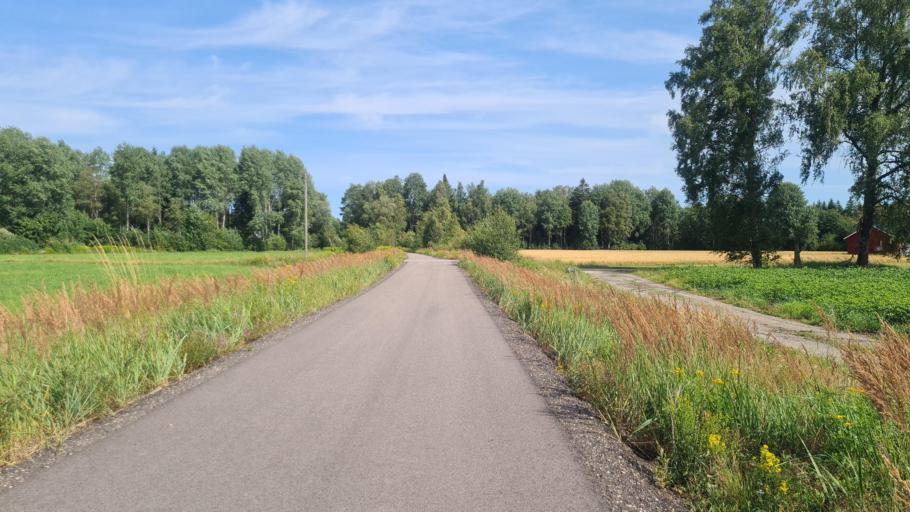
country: SE
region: Kronoberg
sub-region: Ljungby Kommun
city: Lagan
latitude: 56.9044
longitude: 13.9906
